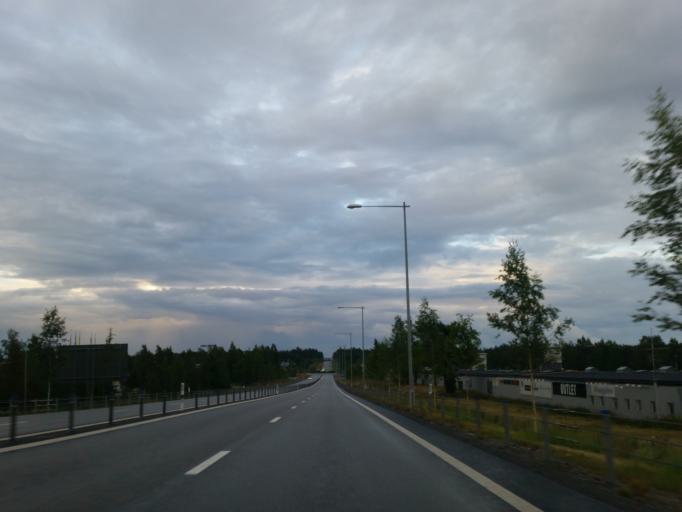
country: SE
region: Vaesterbotten
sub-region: Umea Kommun
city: Ersmark
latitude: 63.8490
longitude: 20.3011
